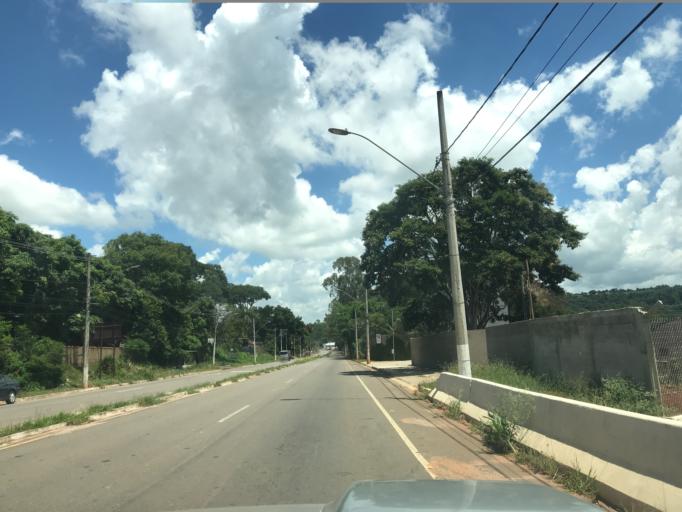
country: BR
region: Minas Gerais
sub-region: Tres Coracoes
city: Tres Coracoes
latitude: -21.6640
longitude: -45.2812
